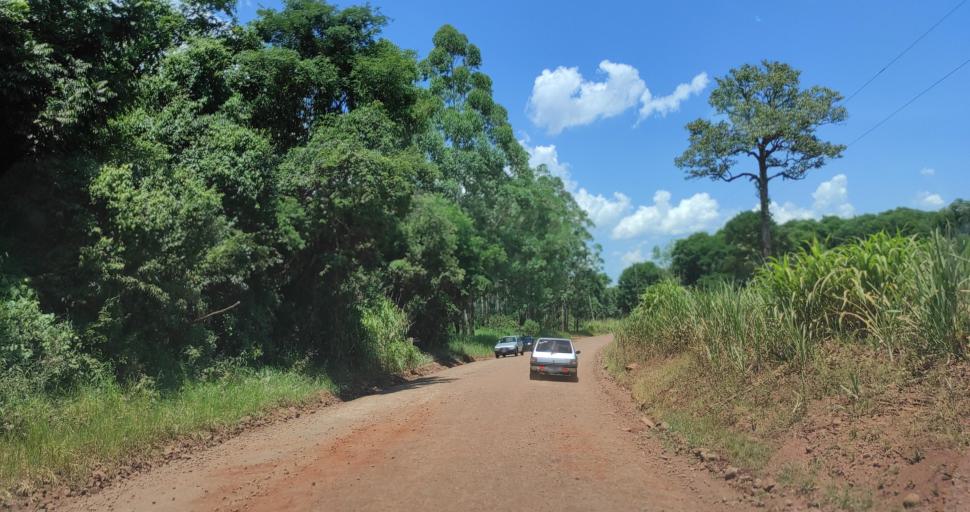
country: AR
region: Misiones
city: Ruiz de Montoya
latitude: -27.0429
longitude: -55.0135
